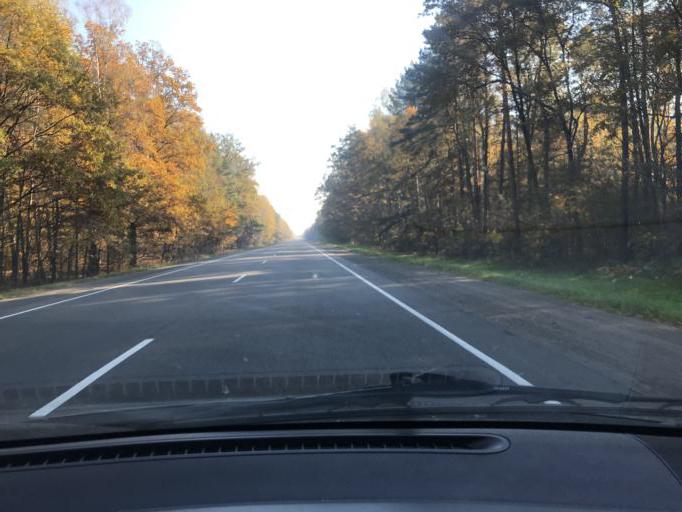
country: BY
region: Brest
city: Horad Luninyets
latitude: 52.2852
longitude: 26.8025
